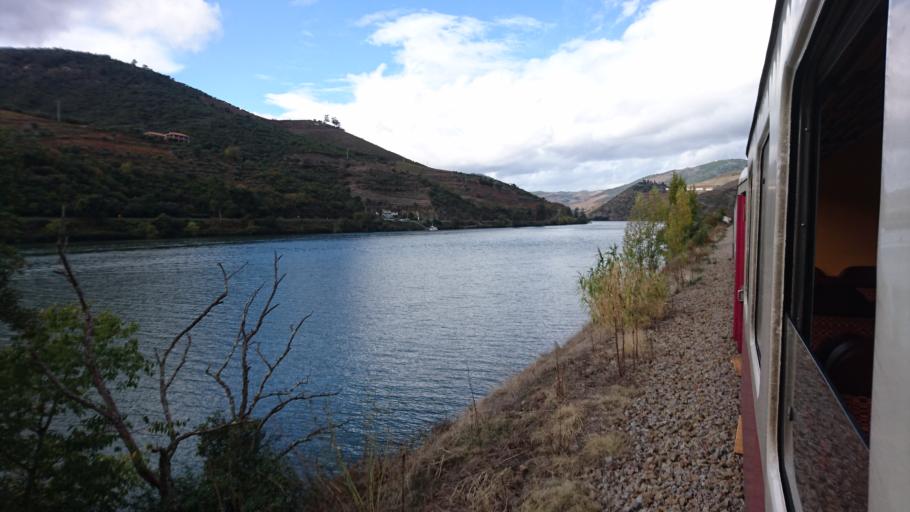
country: PT
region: Viseu
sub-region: Tabuaco
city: Tabuaco
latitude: 41.1592
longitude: -7.5998
